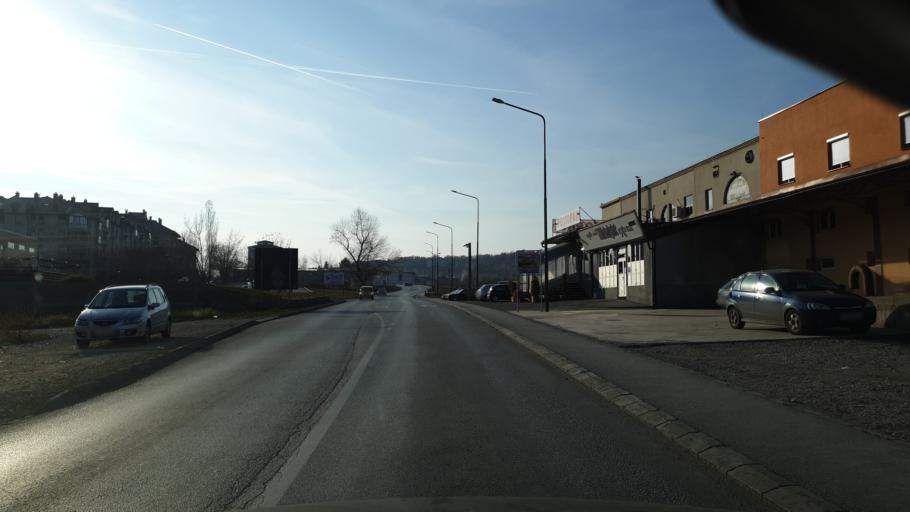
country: RS
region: Central Serbia
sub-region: Borski Okrug
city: Bor
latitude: 44.0582
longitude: 22.1097
